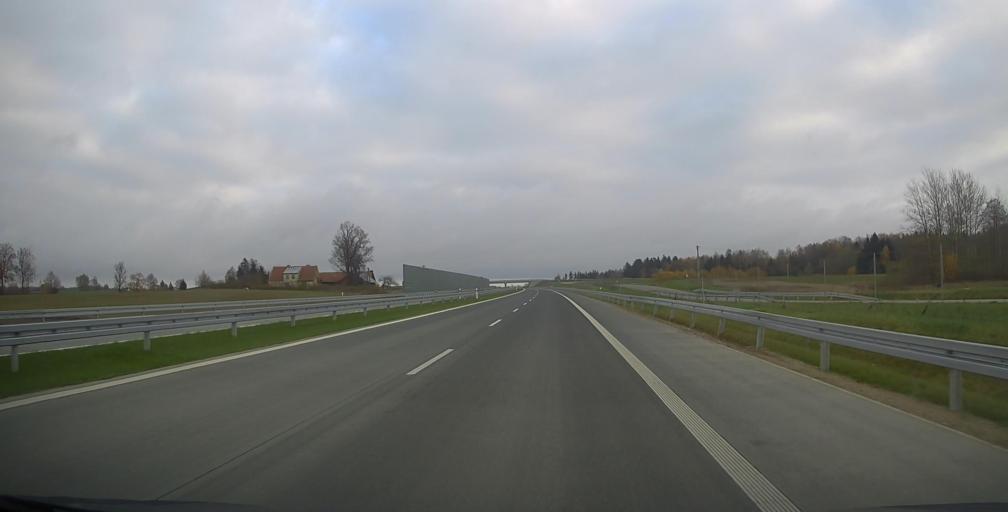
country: PL
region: Podlasie
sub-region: Powiat suwalski
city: Raczki
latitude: 53.9212
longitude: 22.7449
